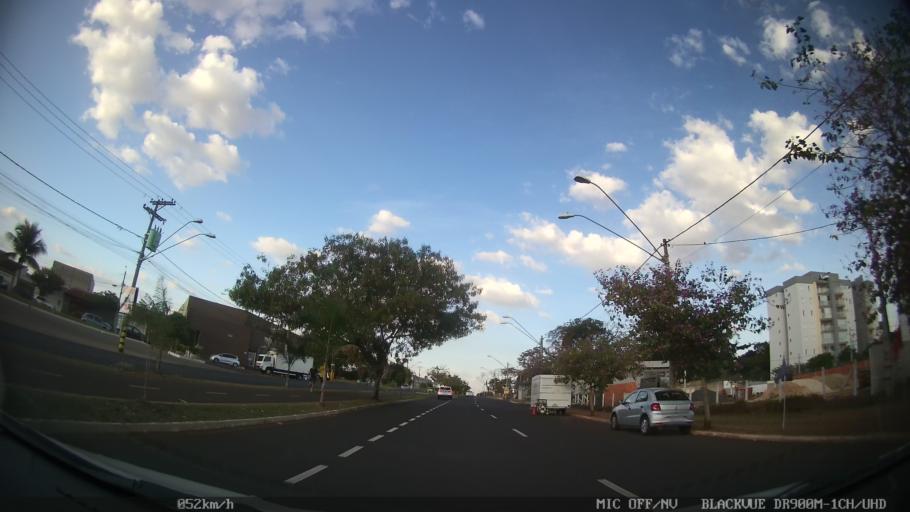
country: BR
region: Sao Paulo
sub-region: Ribeirao Preto
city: Ribeirao Preto
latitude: -21.1936
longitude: -47.7424
